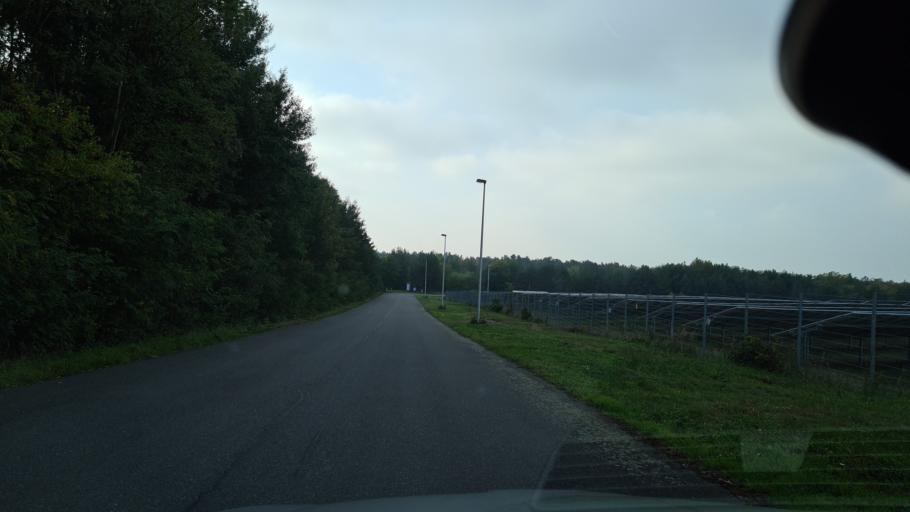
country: DE
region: Brandenburg
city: Elsterwerda
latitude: 51.4801
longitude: 13.4832
